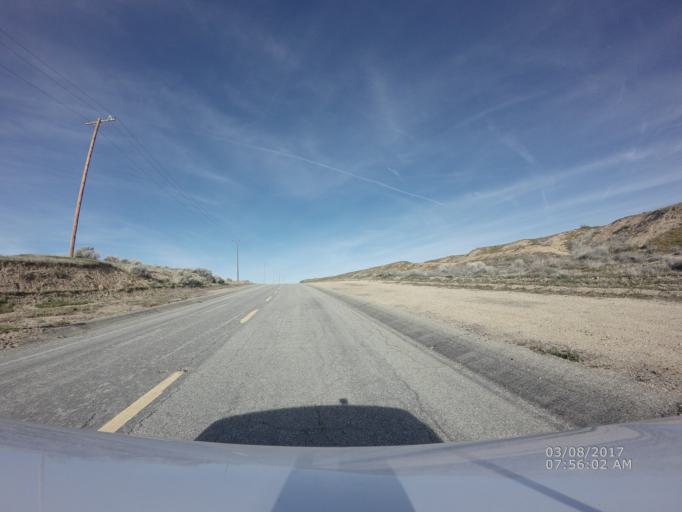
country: US
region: California
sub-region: Los Angeles County
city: Green Valley
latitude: 34.7240
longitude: -118.3864
